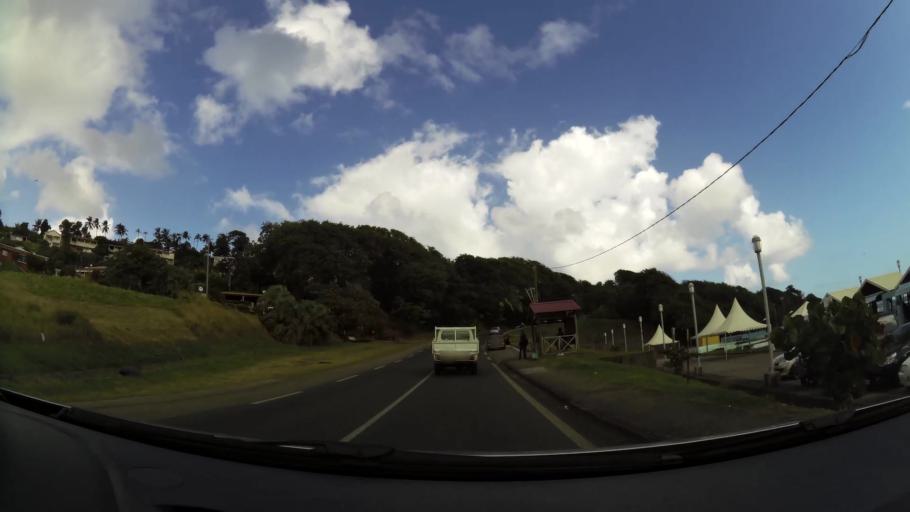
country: MQ
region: Martinique
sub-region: Martinique
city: Le Lorrain
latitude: 14.8238
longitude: -61.0322
